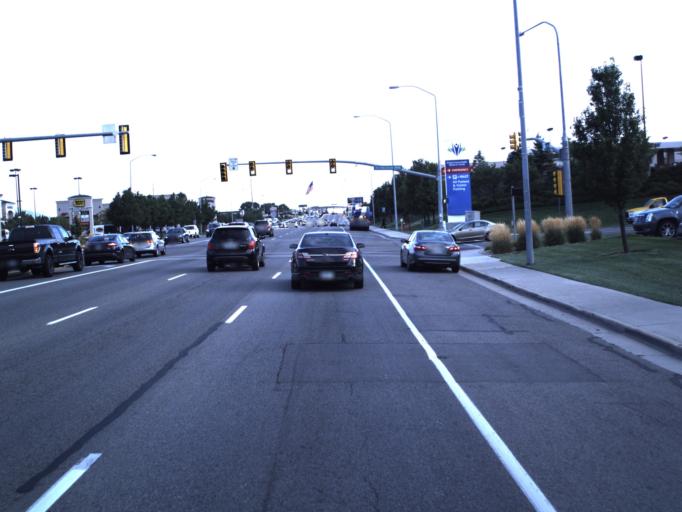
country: US
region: Utah
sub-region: Salt Lake County
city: Murray
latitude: 40.6599
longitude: -111.8884
